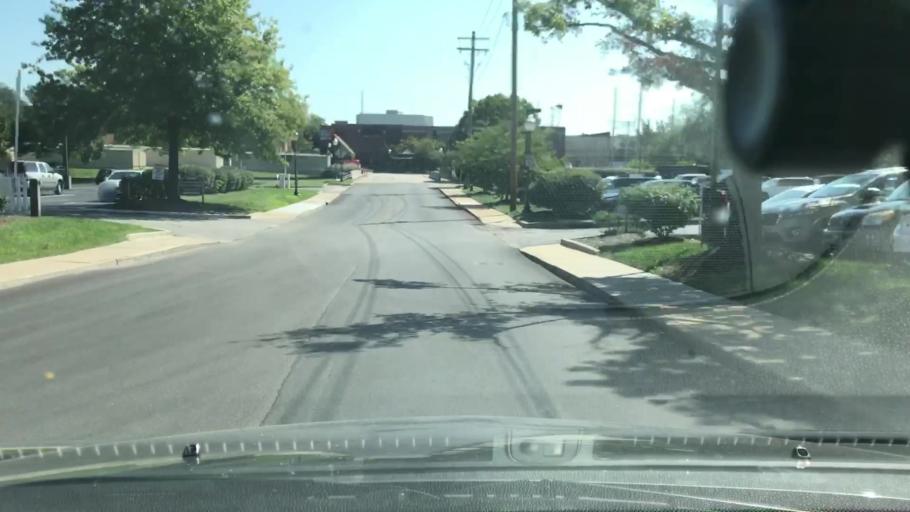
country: US
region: Missouri
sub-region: Saint Louis County
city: Brentwood
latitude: 38.6264
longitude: -90.3456
